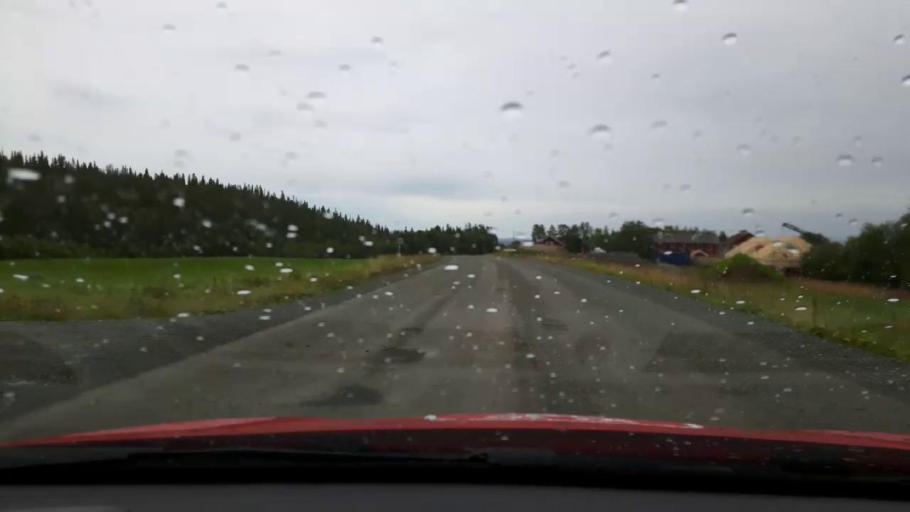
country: SE
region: Jaemtland
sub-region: Are Kommun
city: Are
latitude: 63.4762
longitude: 12.5558
